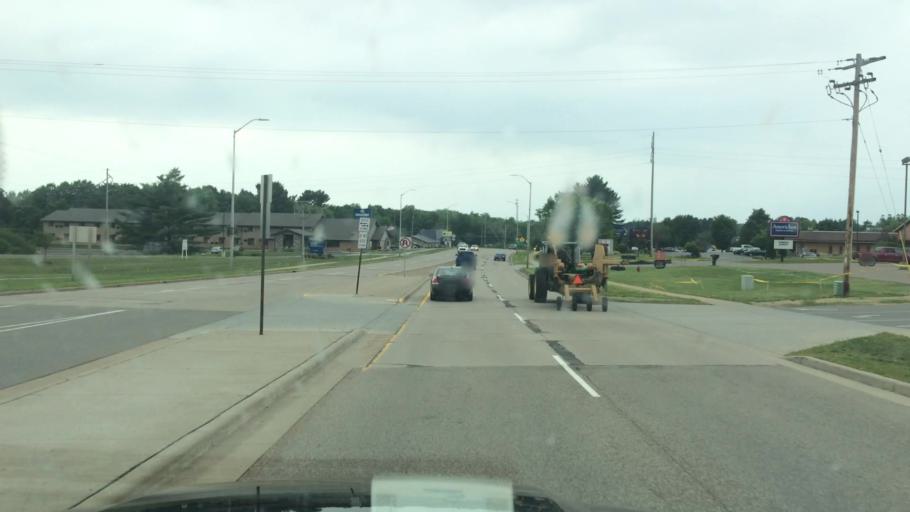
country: US
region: Wisconsin
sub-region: Lincoln County
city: Merrill
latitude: 45.1780
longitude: -89.6529
